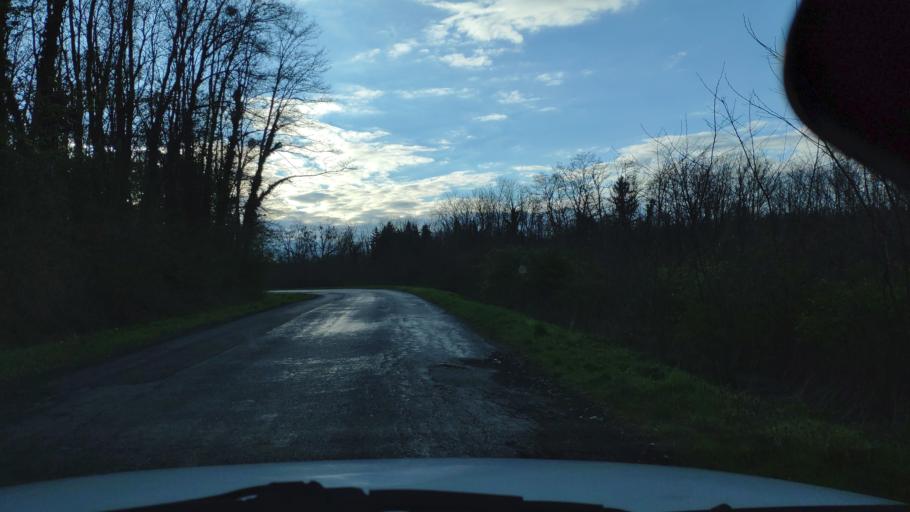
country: HU
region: Zala
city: Nagykanizsa
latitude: 46.4233
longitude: 17.1086
